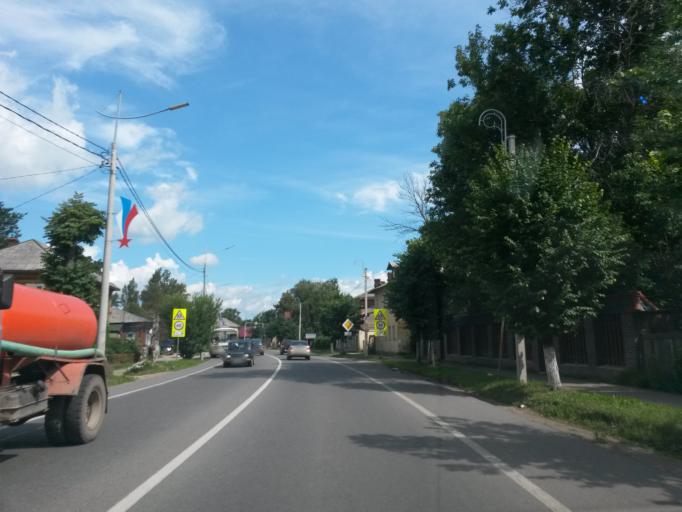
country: RU
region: Jaroslavl
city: Pereslavl'-Zalesskiy
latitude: 56.7291
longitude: 38.8453
